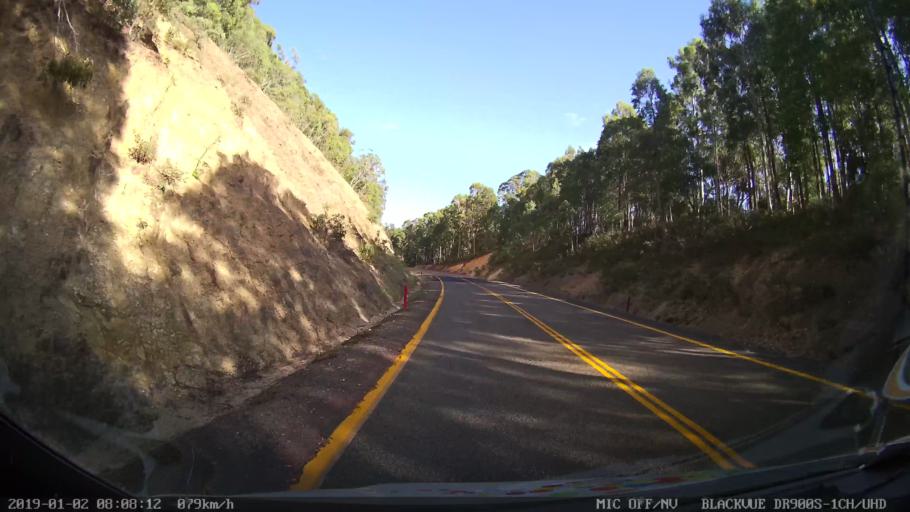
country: AU
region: New South Wales
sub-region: Tumut Shire
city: Tumut
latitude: -35.6183
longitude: 148.3879
